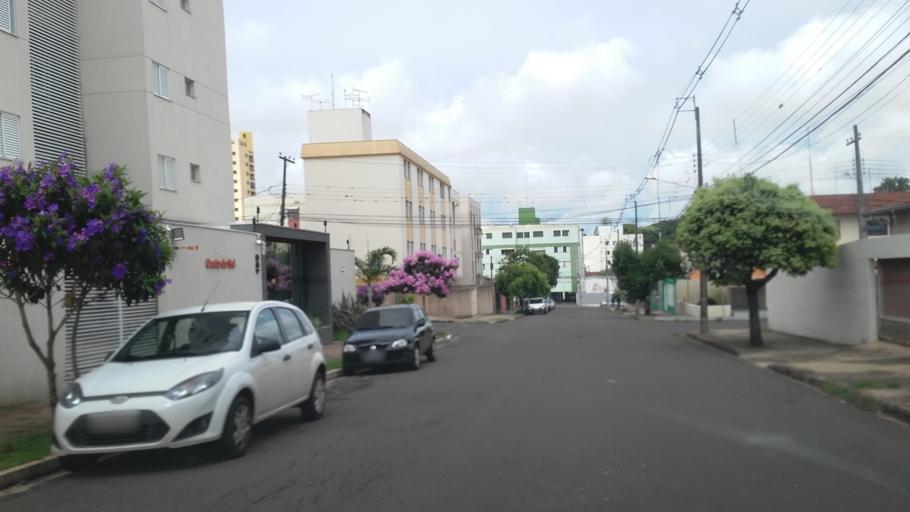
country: BR
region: Parana
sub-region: Londrina
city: Londrina
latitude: -23.3036
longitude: -51.1775
